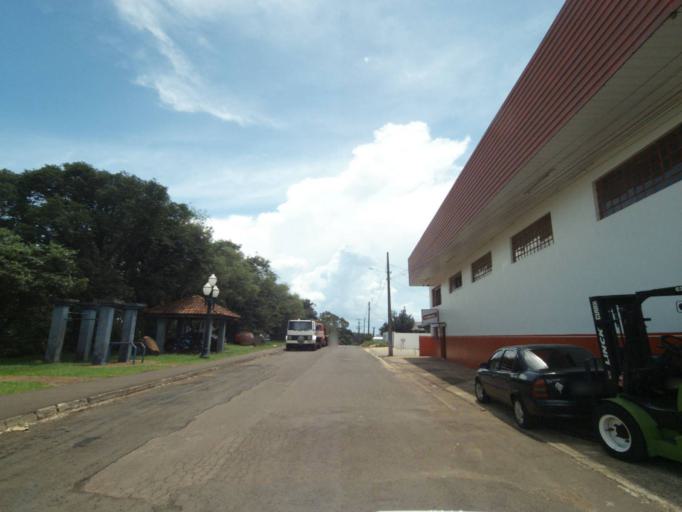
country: BR
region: Parana
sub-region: Guaraniacu
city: Guaraniacu
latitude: -25.0963
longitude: -52.8767
